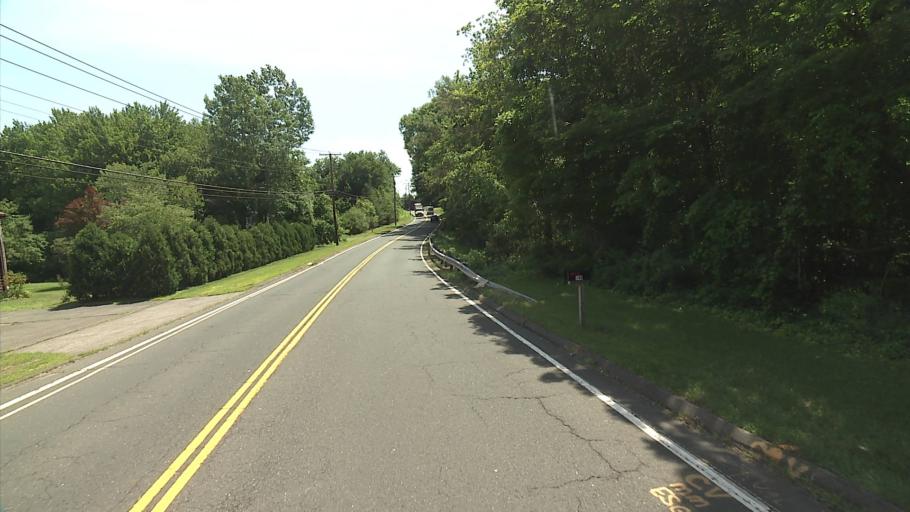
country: US
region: Connecticut
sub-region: Middlesex County
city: Cromwell
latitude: 41.6054
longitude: -72.6660
